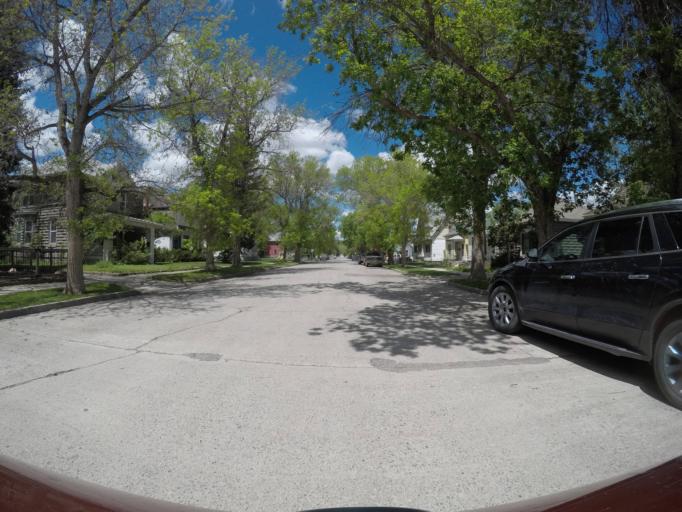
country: US
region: Montana
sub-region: Park County
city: Livingston
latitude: 45.6587
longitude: -110.5606
